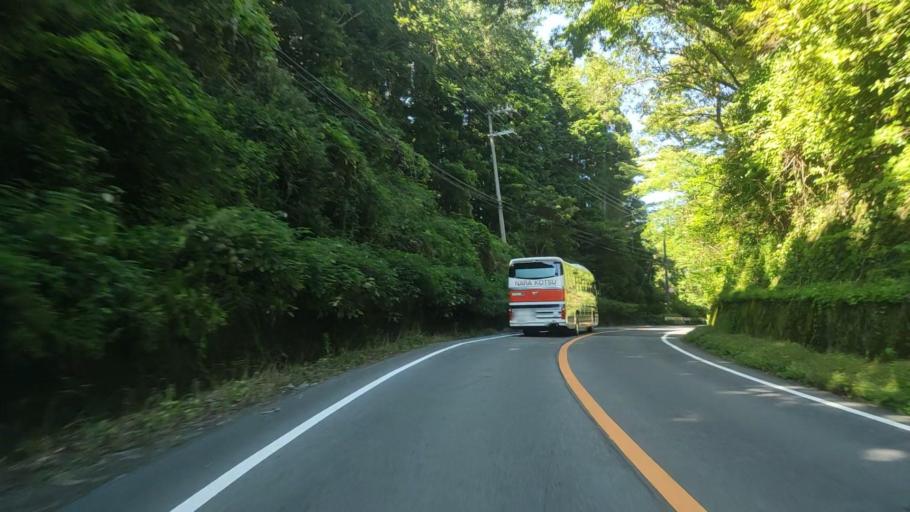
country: JP
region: Nara
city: Haibara-akanedai
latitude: 34.5316
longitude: 135.9437
